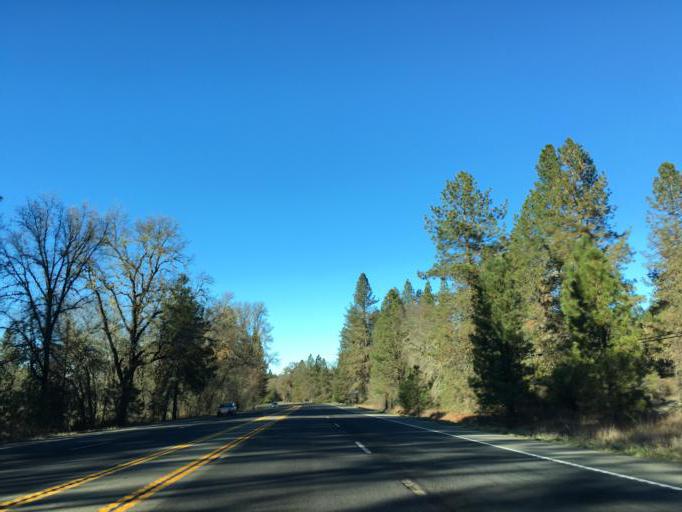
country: US
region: California
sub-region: Mendocino County
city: Laytonville
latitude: 39.7249
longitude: -123.5034
